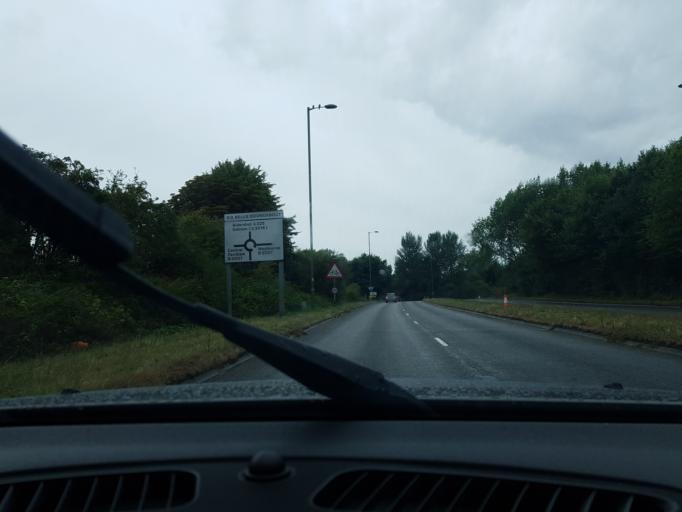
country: GB
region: England
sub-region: Surrey
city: Hale
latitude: 51.2236
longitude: -0.7812
